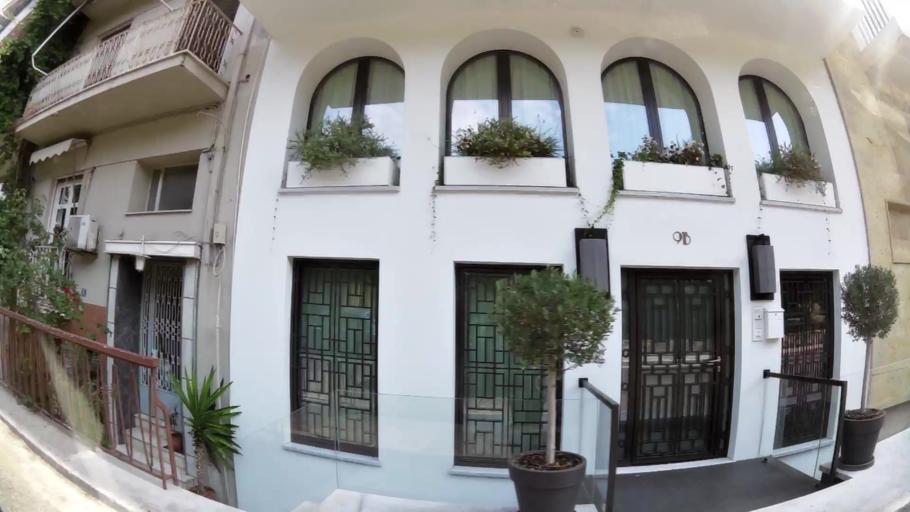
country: GR
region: Attica
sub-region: Nomarchia Athinas
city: Athens
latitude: 37.9690
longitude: 23.7237
